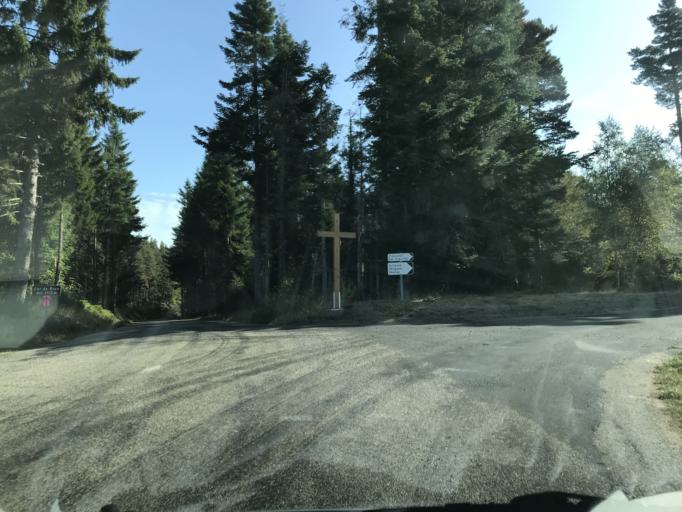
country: FR
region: Rhone-Alpes
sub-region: Departement de l'Ardeche
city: Saint-Agreve
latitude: 45.0364
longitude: 4.4432
